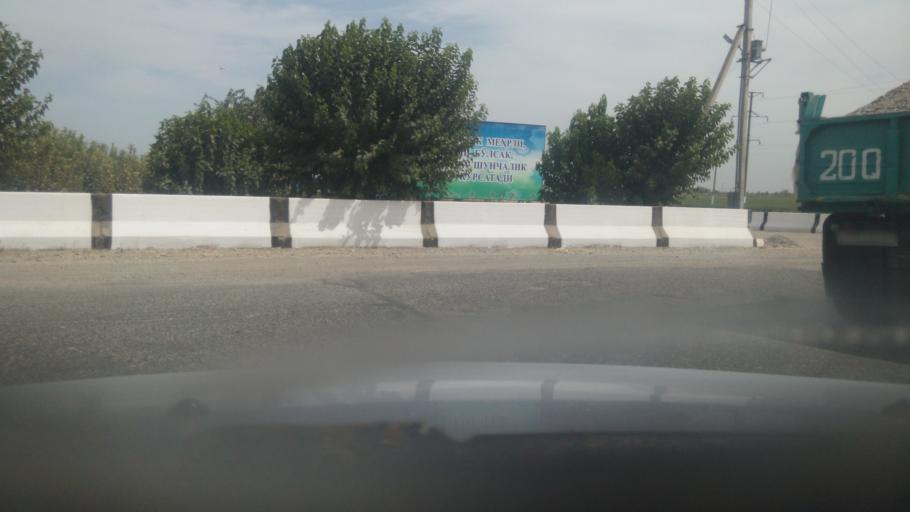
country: UZ
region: Sirdaryo
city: Guliston
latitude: 40.5173
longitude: 68.7933
